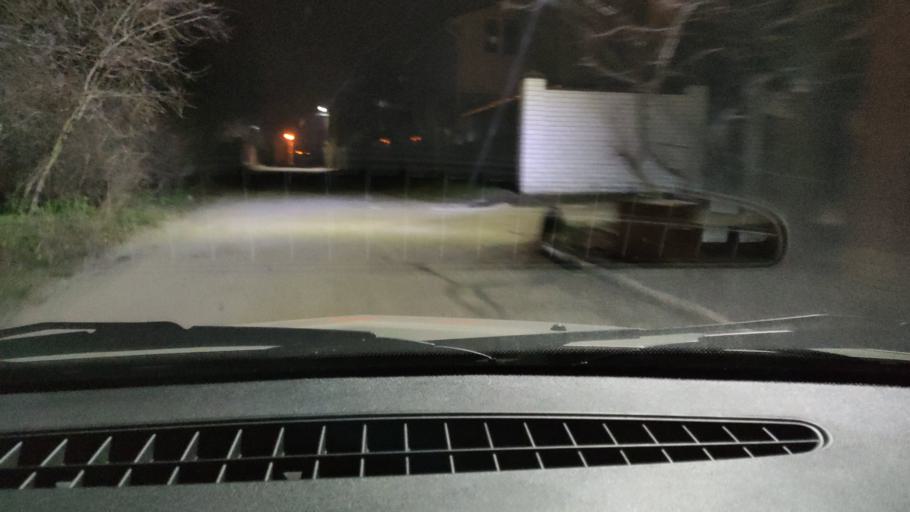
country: RU
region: Voronezj
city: Pridonskoy
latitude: 51.6384
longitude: 39.0846
